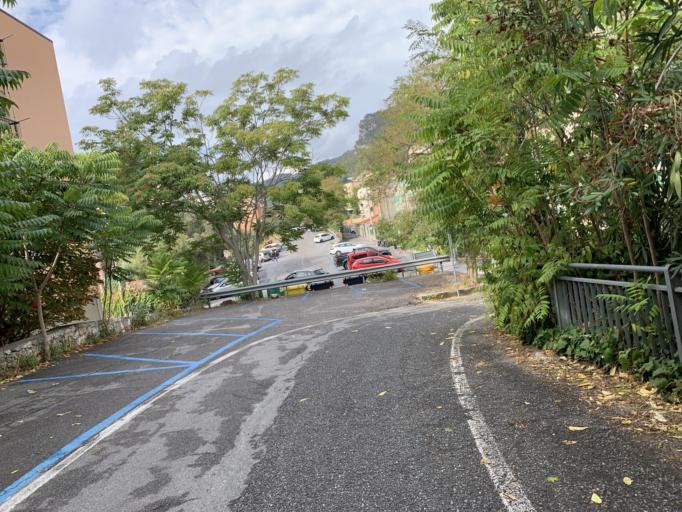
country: IT
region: Liguria
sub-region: Provincia di Savona
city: Noli
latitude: 44.1824
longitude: 8.3945
